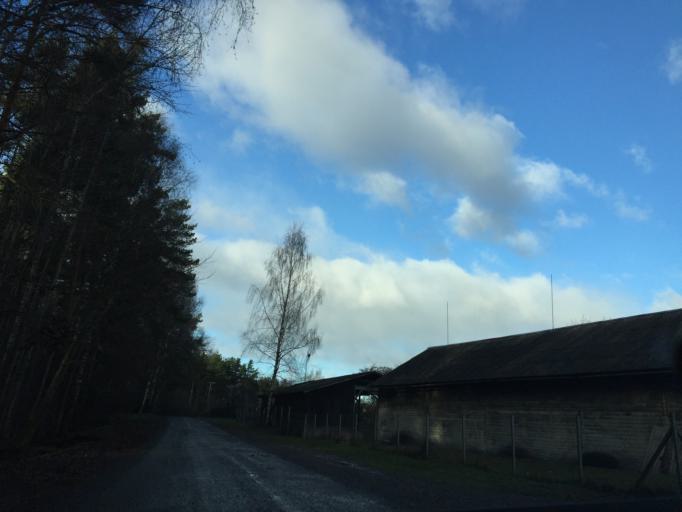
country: LV
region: Valmieras Rajons
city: Valmiera
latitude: 57.5313
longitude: 25.3833
